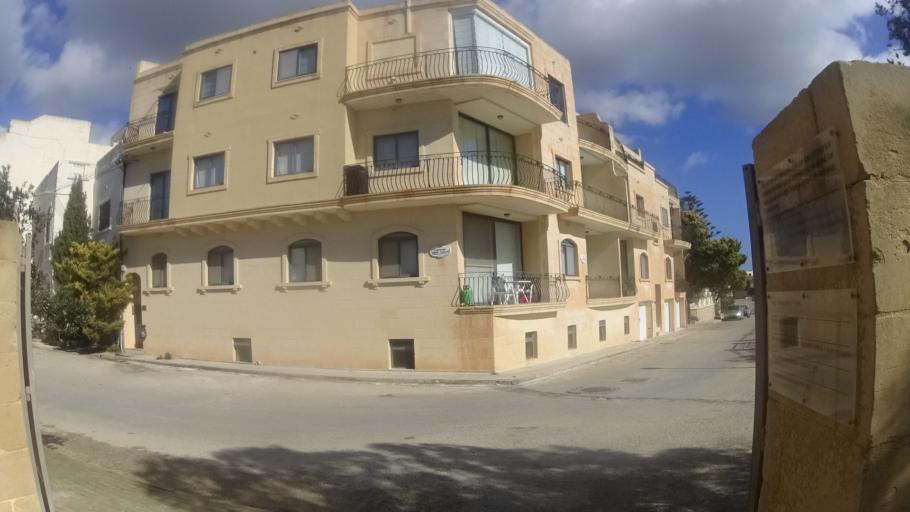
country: MT
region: Ghajnsielem
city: Ghajnsielem
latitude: 36.0356
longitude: 14.2845
